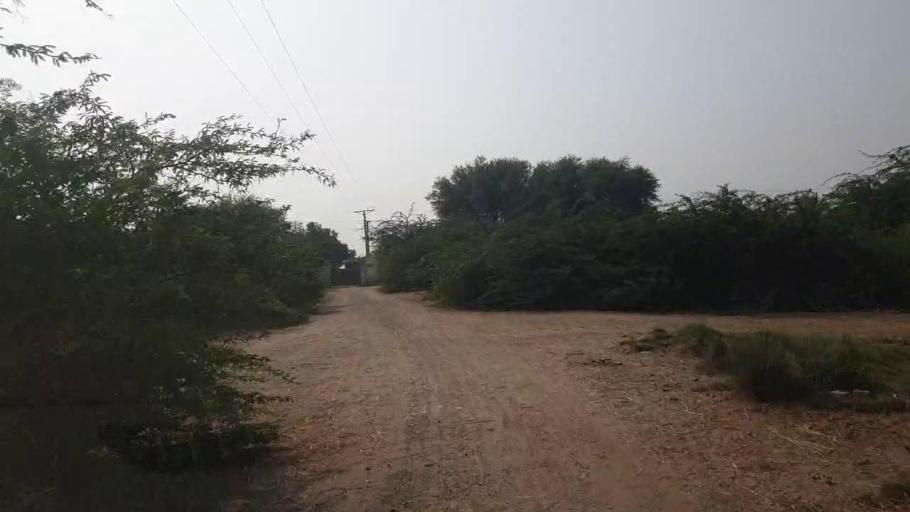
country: PK
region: Sindh
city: Tando Muhammad Khan
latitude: 25.2600
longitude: 68.5109
